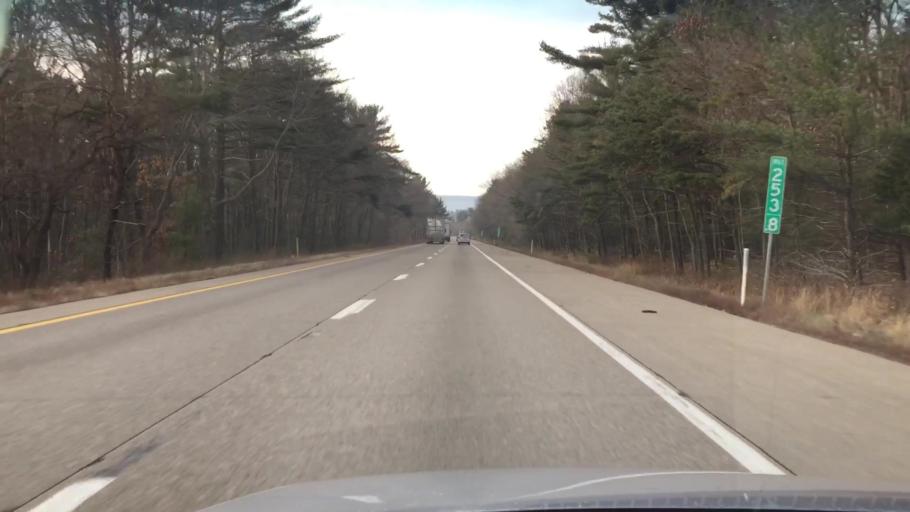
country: US
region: Pennsylvania
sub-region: Luzerne County
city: Conyngham
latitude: 41.0175
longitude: -76.1164
